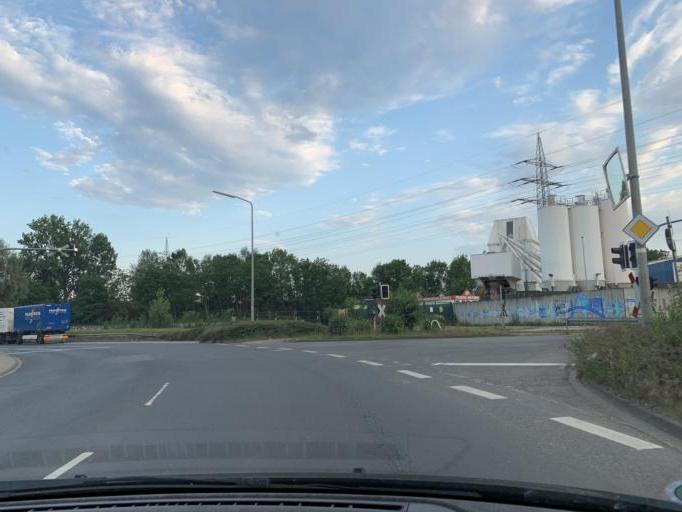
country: DE
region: North Rhine-Westphalia
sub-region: Regierungsbezirk Dusseldorf
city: Dusseldorf
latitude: 51.2110
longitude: 6.7340
